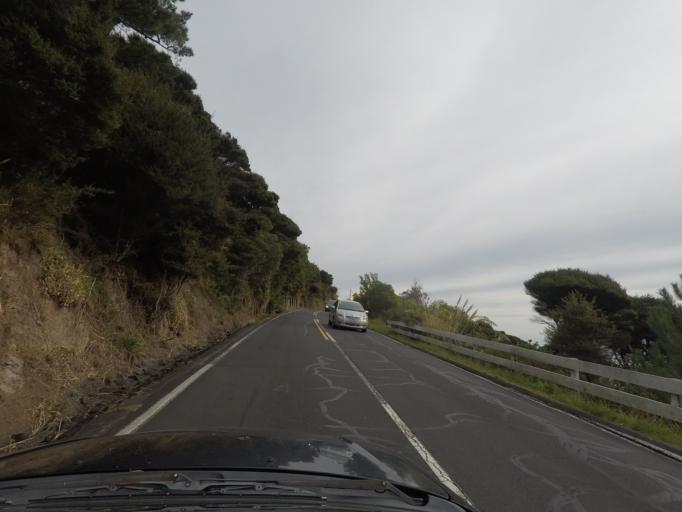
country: NZ
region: Auckland
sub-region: Auckland
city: Muriwai Beach
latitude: -36.9610
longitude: 174.4762
